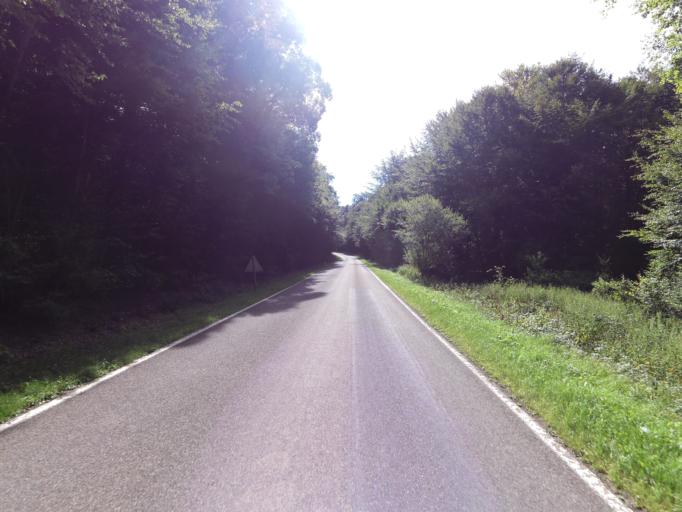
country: BE
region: Wallonia
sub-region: Province du Luxembourg
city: Nassogne
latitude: 50.0793
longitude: 5.3432
